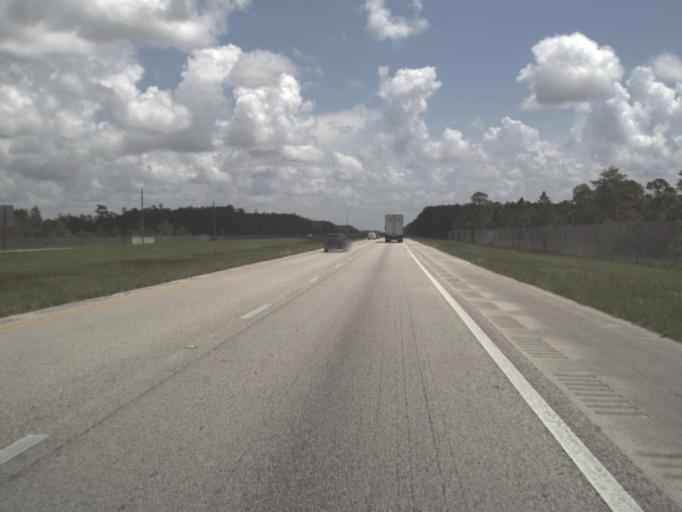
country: US
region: Florida
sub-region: Collier County
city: Immokalee
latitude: 26.1672
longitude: -81.1753
